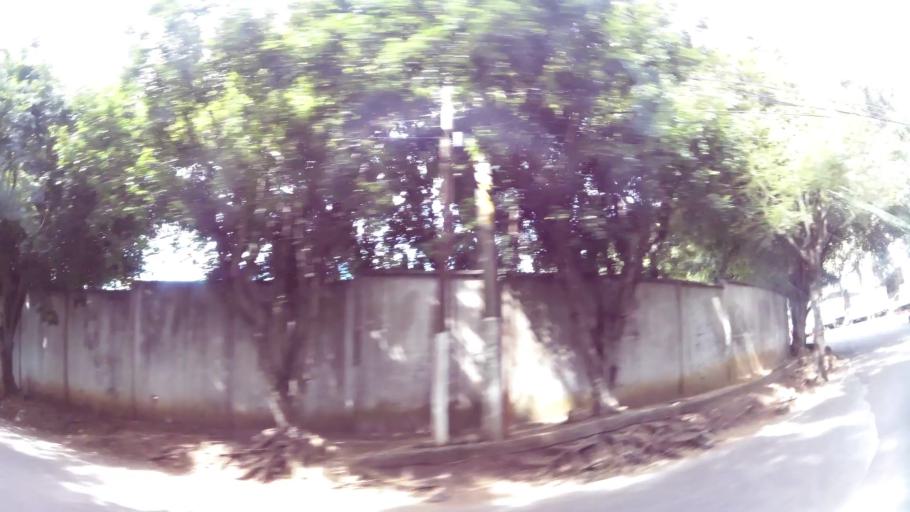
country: GT
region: Guatemala
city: Santa Catarina Pinula
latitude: 14.5838
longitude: -90.5294
